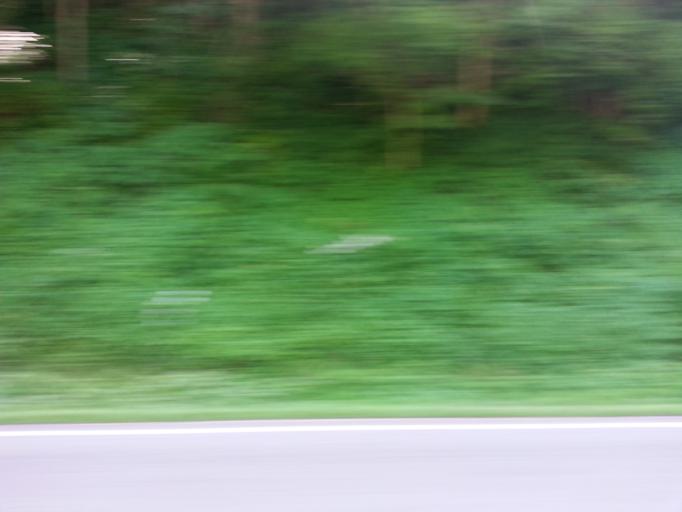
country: US
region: Virginia
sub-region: Lee County
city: Pennington Gap
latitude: 36.7495
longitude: -83.0091
